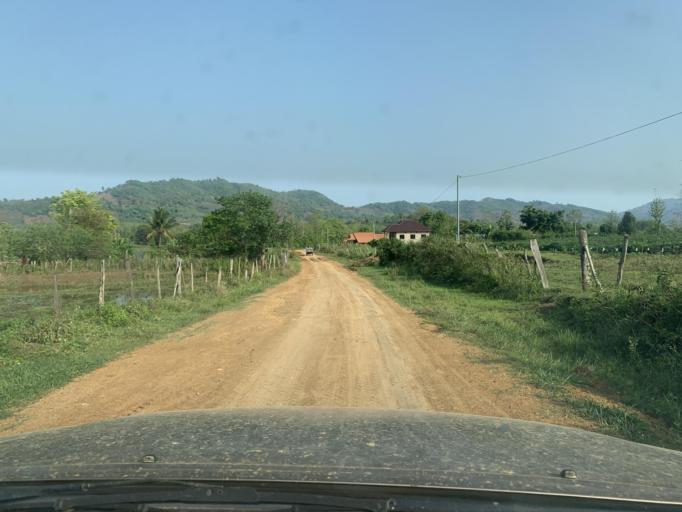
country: TH
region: Uttaradit
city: Ban Khok
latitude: 18.2719
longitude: 101.3074
